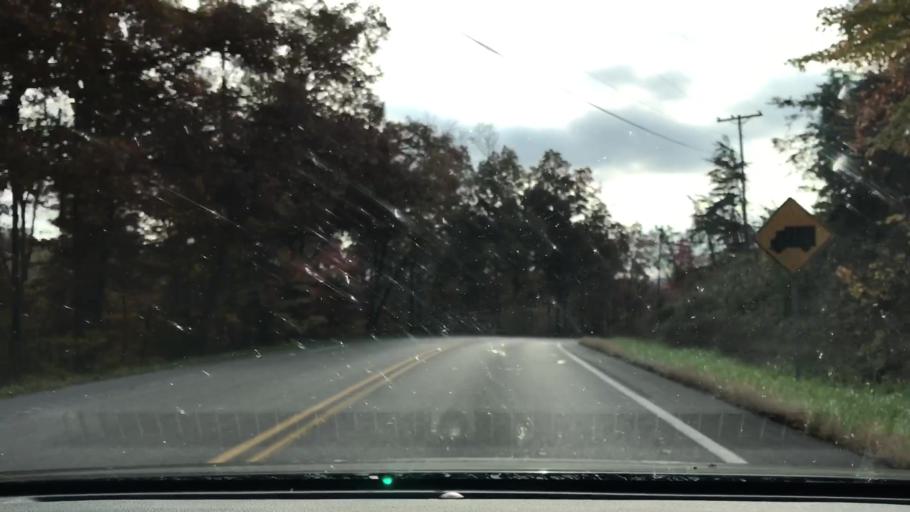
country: US
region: Tennessee
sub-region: Putnam County
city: Monterey
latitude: 36.1281
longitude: -85.2021
